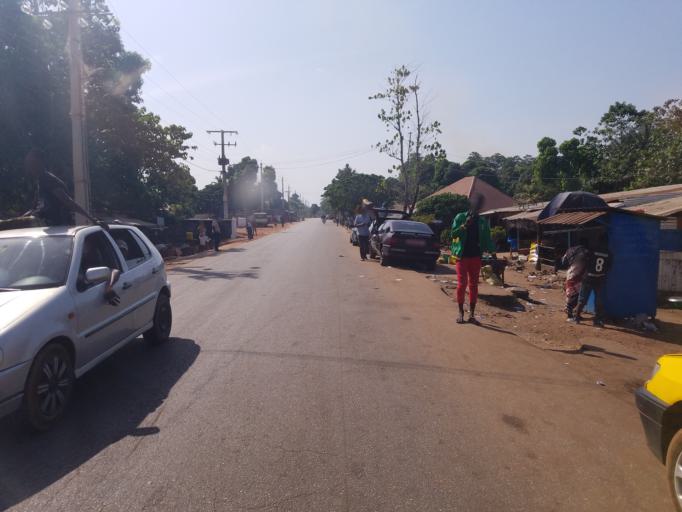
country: GN
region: Boke
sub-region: Fria
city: Fria
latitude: 10.0816
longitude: -13.6928
